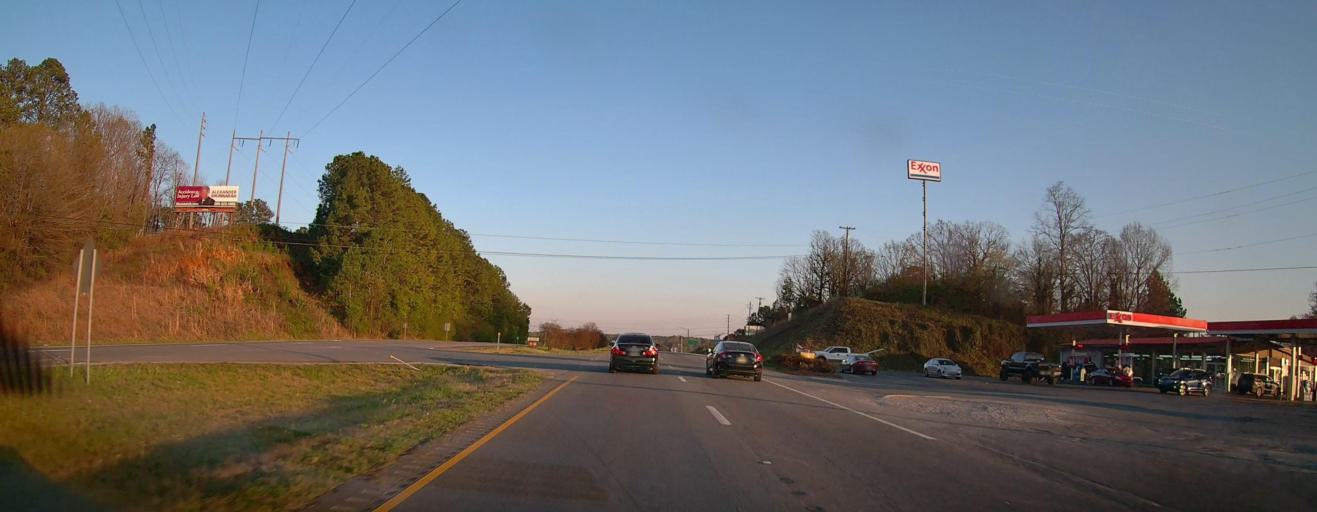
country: US
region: Alabama
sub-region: Talladega County
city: Mignon
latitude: 33.1661
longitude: -86.2776
